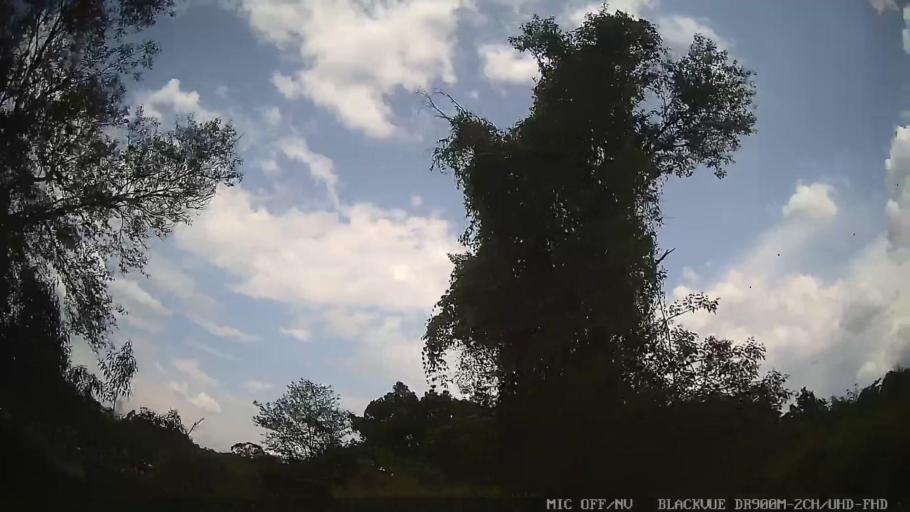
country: BR
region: Sao Paulo
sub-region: Louveira
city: Louveira
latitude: -23.1212
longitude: -46.9638
